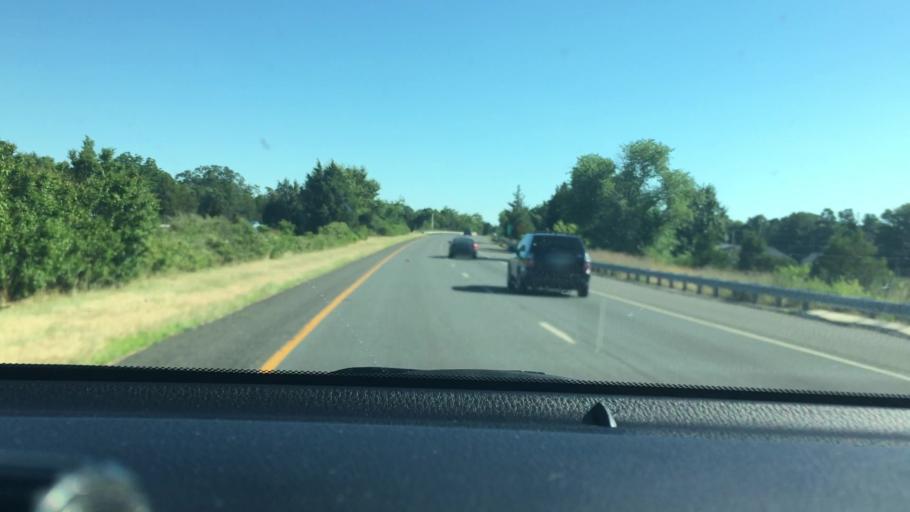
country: US
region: New Jersey
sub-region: Gloucester County
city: Newfield
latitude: 39.5504
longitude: -75.0583
